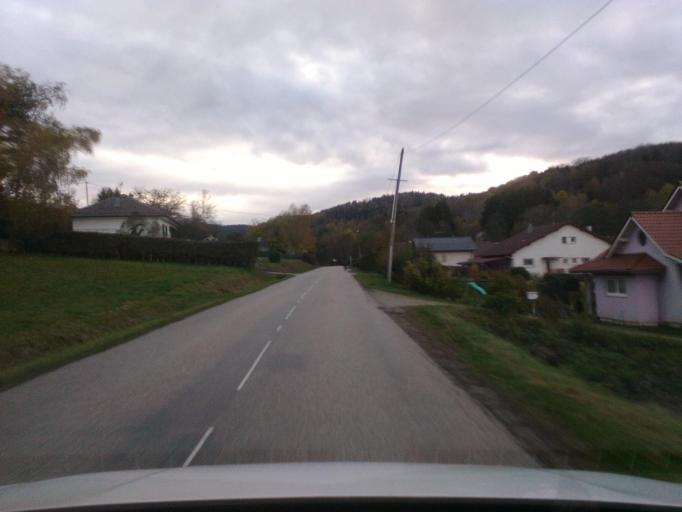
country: FR
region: Lorraine
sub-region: Departement des Vosges
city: Ban-de-Laveline
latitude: 48.2269
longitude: 7.0565
